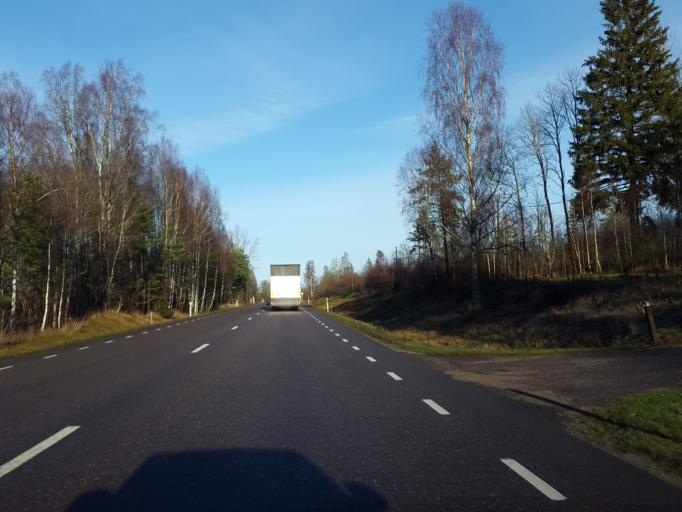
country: SE
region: Vaestra Goetaland
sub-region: Vargarda Kommun
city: Vargarda
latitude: 58.0080
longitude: 12.8162
